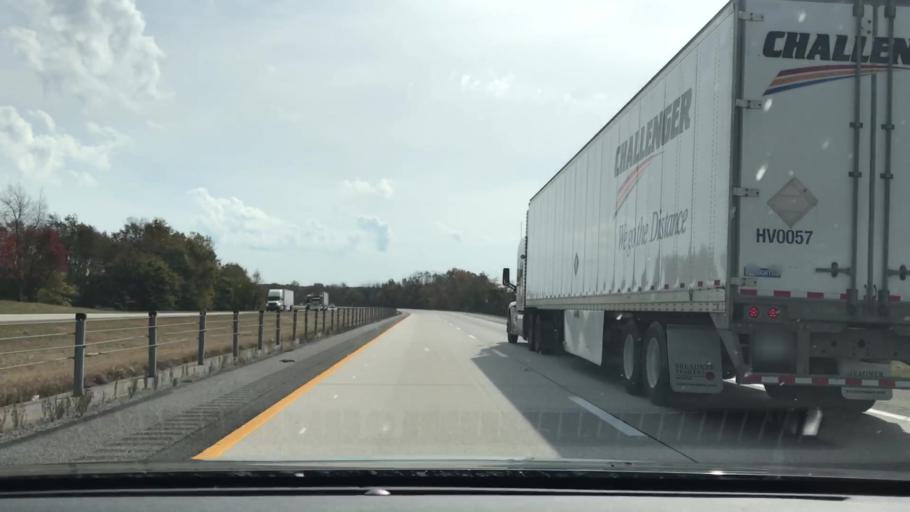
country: US
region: Kentucky
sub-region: Trigg County
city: Cadiz
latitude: 36.8586
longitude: -87.7053
